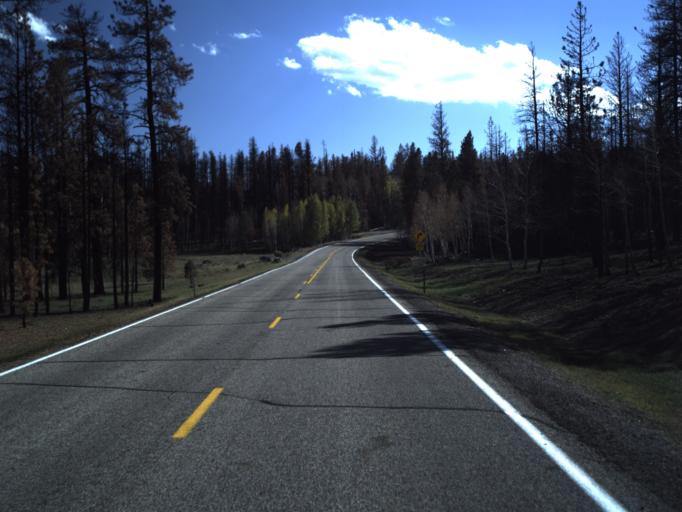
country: US
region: Utah
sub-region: Iron County
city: Parowan
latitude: 37.6619
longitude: -112.6657
